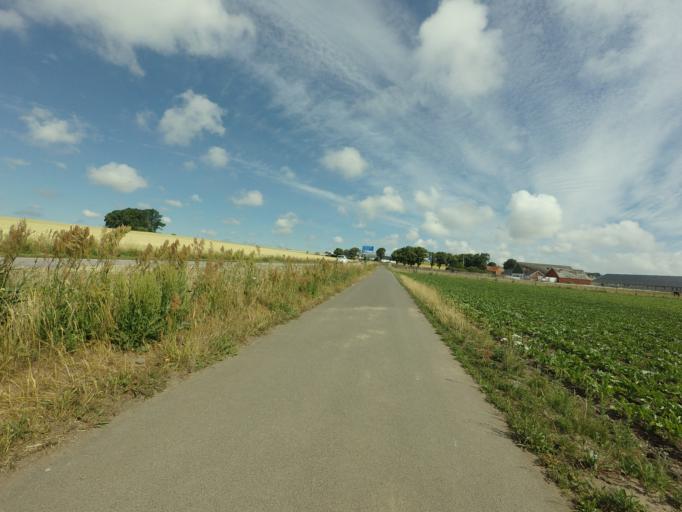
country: SE
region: Skane
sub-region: Simrishamns Kommun
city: Simrishamn
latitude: 55.4815
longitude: 14.2847
